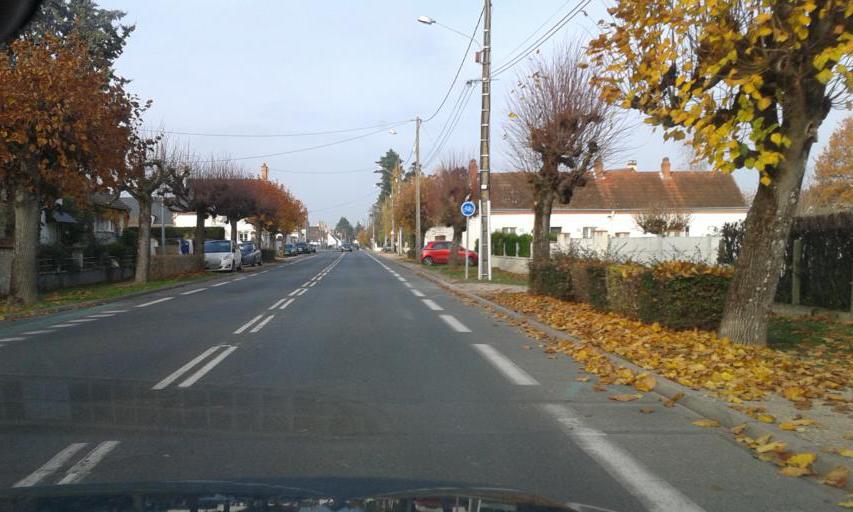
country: FR
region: Centre
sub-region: Departement du Loiret
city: Olivet
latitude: 47.8553
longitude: 1.9043
